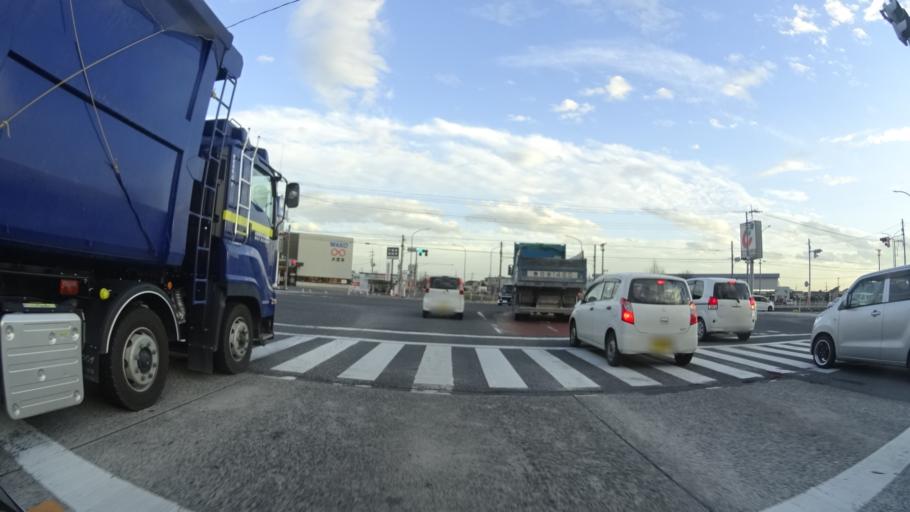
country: JP
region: Tochigi
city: Tochigi
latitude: 36.3936
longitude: 139.7247
